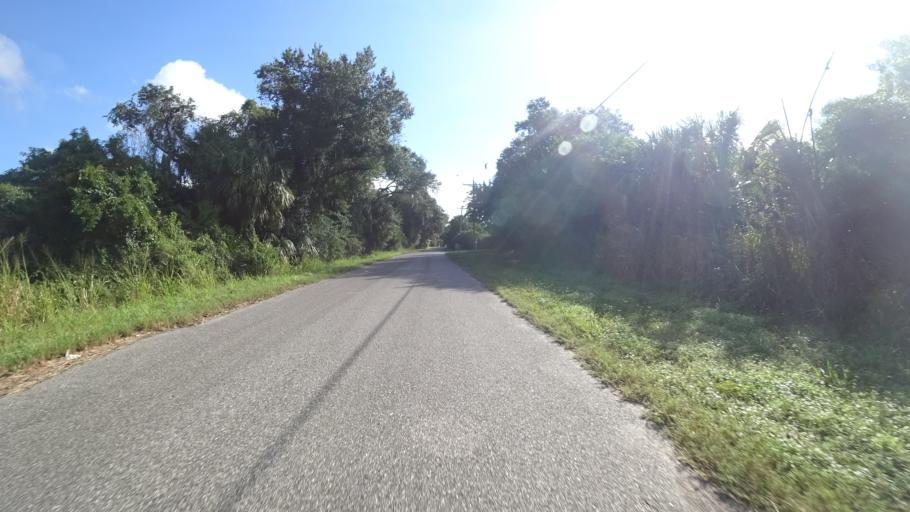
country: US
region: Florida
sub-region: Manatee County
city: Ellenton
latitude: 27.5830
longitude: -82.5096
